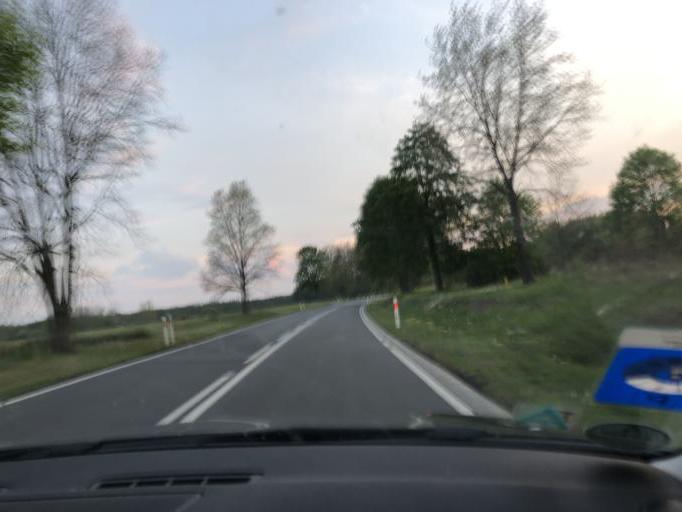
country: PL
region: Lubusz
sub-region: Powiat zarski
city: Trzebiel
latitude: 51.6272
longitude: 14.8087
